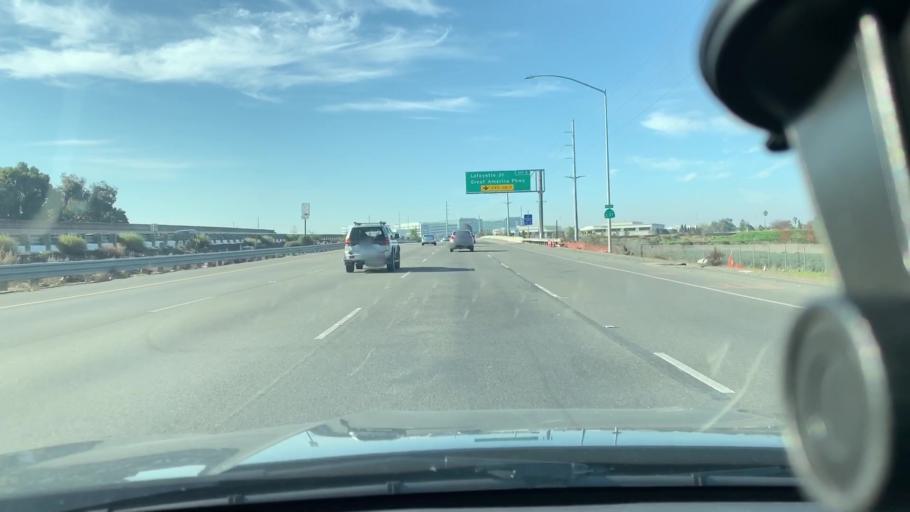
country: US
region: California
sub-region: Santa Clara County
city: Milpitas
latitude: 37.4193
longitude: -121.9649
